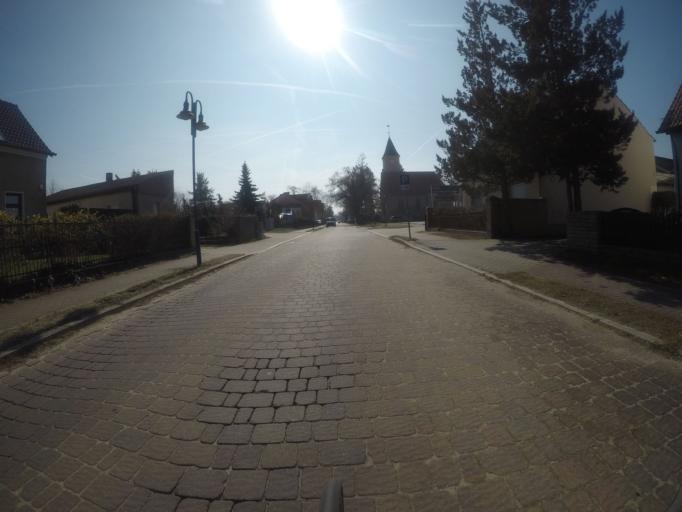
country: DE
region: Brandenburg
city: Erkner
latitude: 52.3949
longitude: 13.7128
